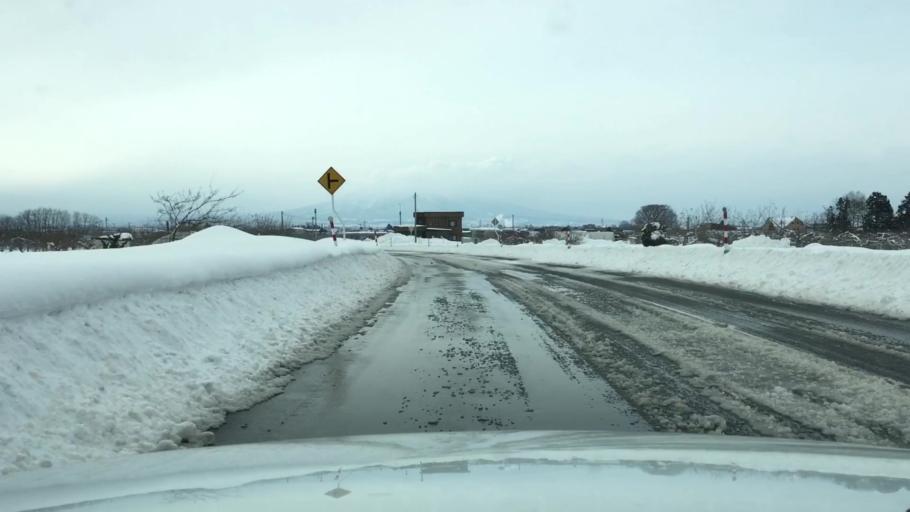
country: JP
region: Aomori
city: Kuroishi
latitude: 40.5931
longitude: 140.5982
